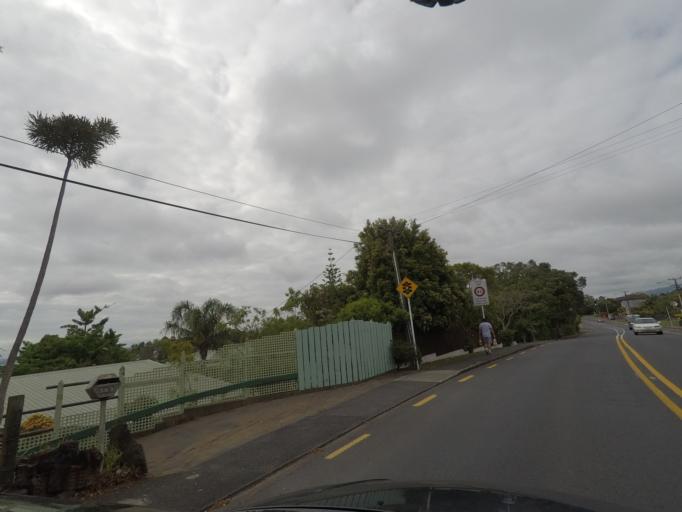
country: NZ
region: Auckland
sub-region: Auckland
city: Rosebank
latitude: -36.8390
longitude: 174.6005
